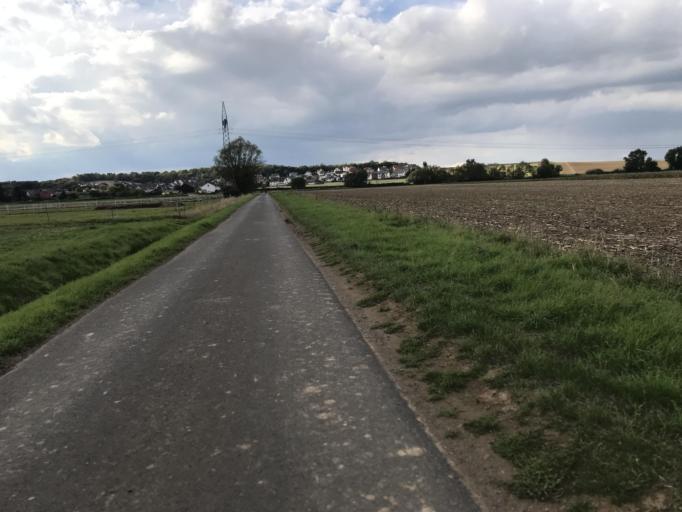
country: DE
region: Hesse
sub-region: Regierungsbezirk Kassel
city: Wabern
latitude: 51.0833
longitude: 9.3474
